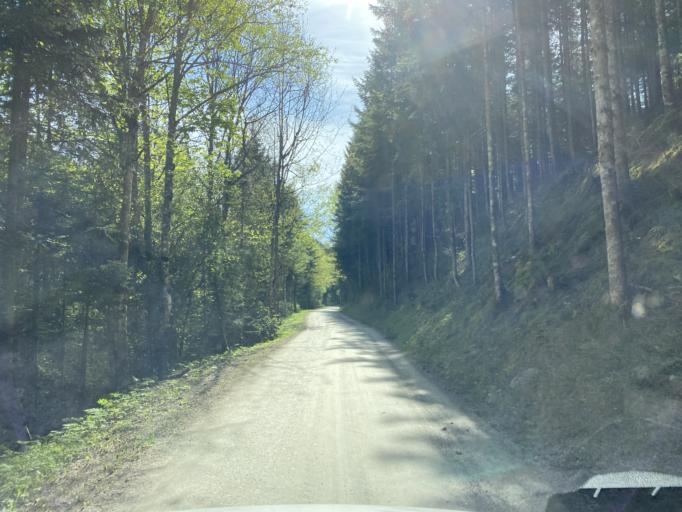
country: AT
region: Styria
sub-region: Politischer Bezirk Weiz
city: Birkfeld
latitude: 47.3432
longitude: 15.7046
